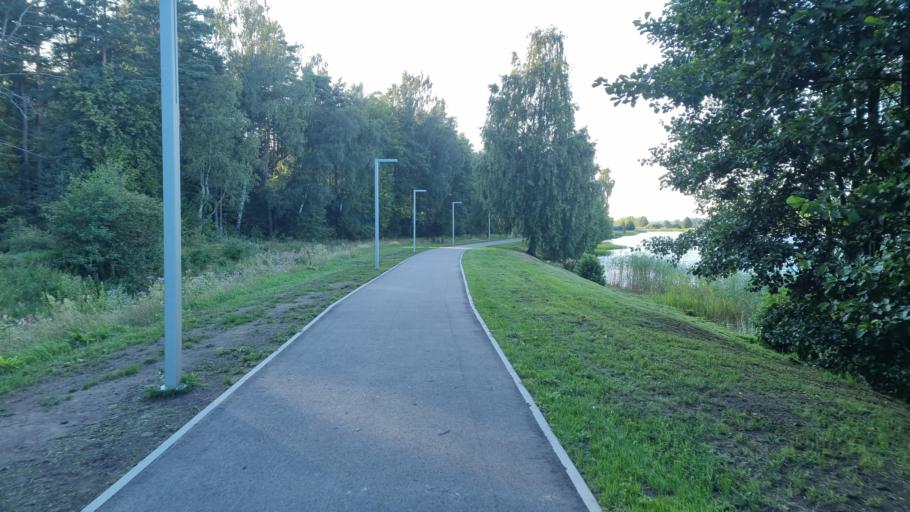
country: LV
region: Babite
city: Pinki
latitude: 56.9379
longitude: 23.9076
